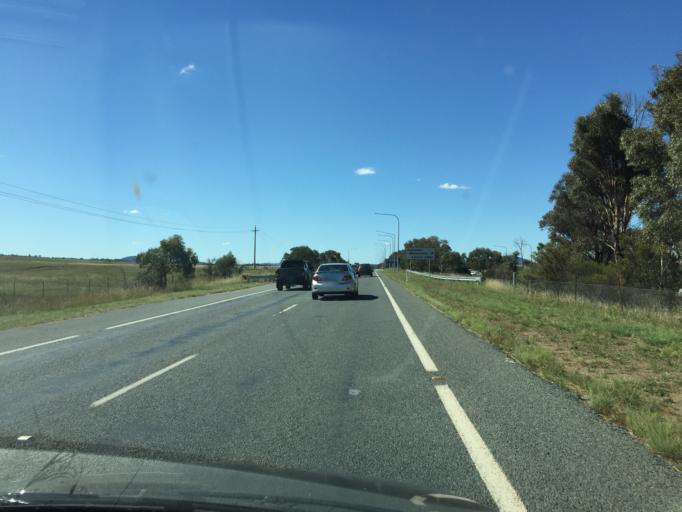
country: AU
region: Australian Capital Territory
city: Macarthur
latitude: -35.3752
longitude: 149.1689
